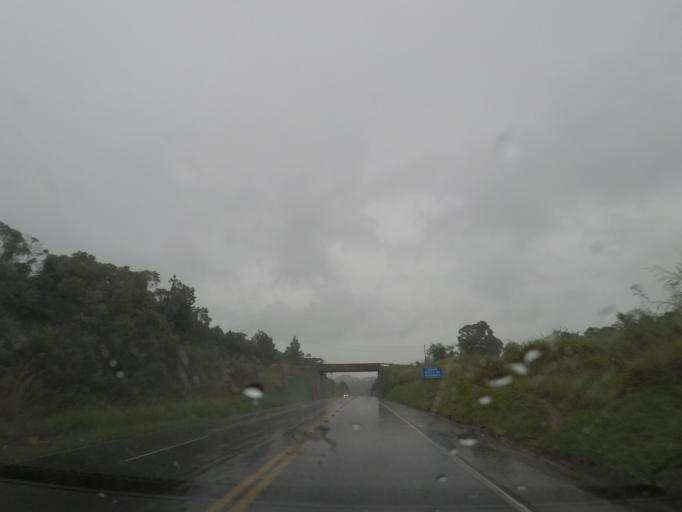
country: BR
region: Parana
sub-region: Almirante Tamandare
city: Almirante Tamandare
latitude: -25.3596
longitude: -49.3130
